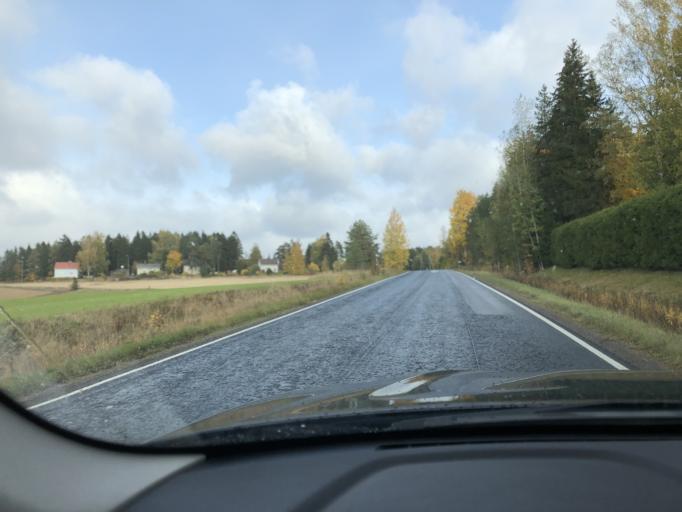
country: FI
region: Pirkanmaa
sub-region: Etelae-Pirkanmaa
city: Toijala
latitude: 61.1403
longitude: 23.8429
